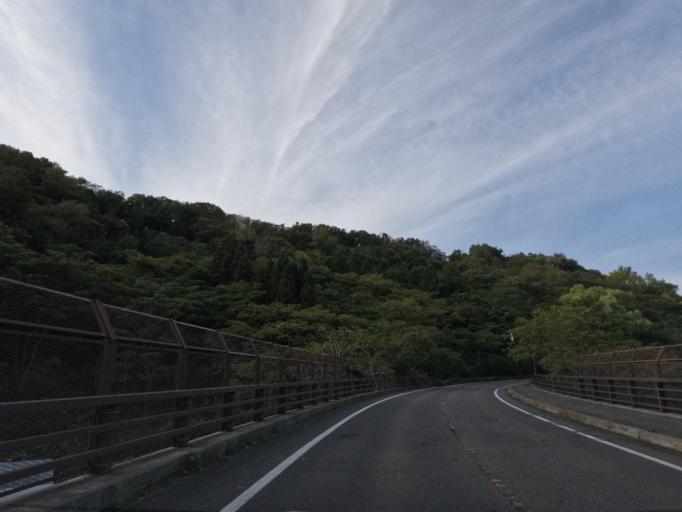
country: JP
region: Hokkaido
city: Date
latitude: 42.5214
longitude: 140.8610
